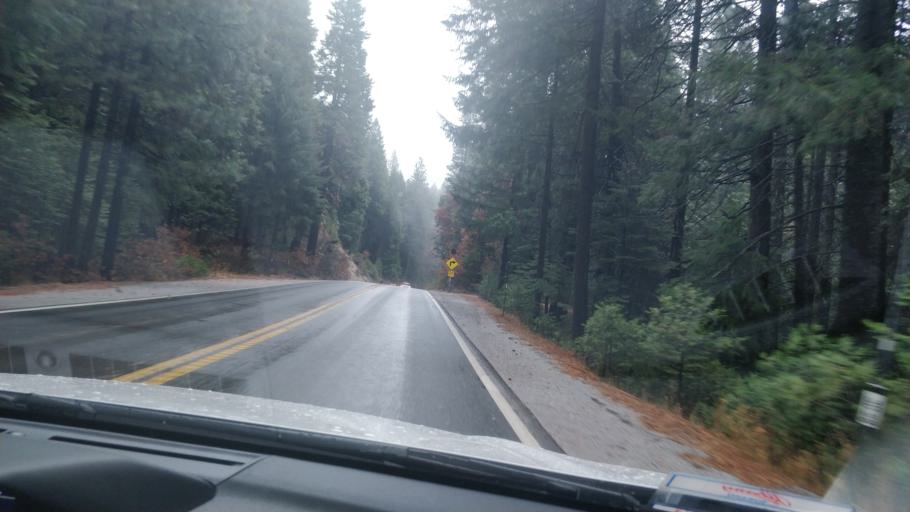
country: US
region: California
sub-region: Nevada County
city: Nevada City
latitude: 39.3225
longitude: -120.8353
